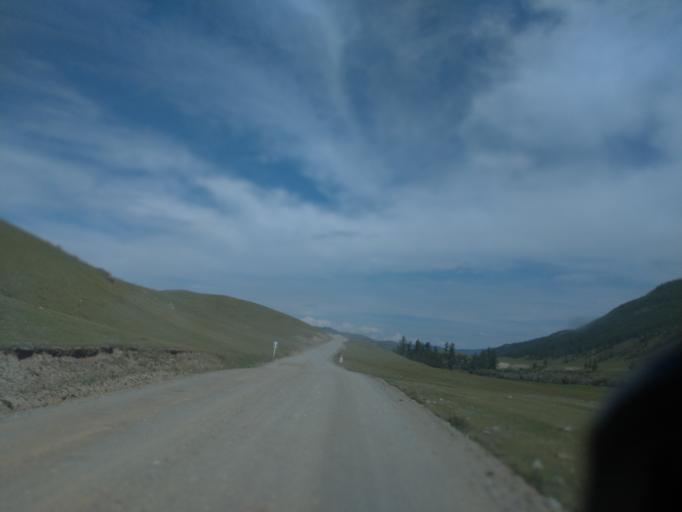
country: RU
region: Altay
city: Ust'-Ulagan
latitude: 50.7075
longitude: 88.0176
